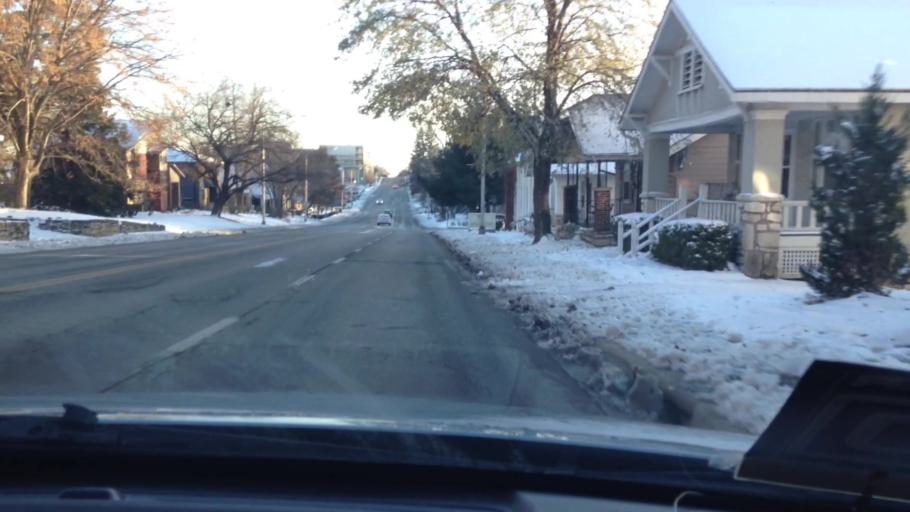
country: US
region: Kansas
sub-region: Johnson County
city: Westwood
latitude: 39.0485
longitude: -94.6120
